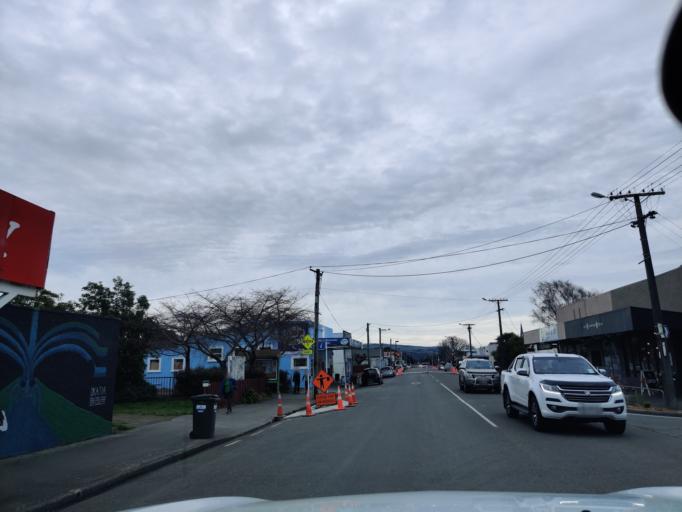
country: NZ
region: Manawatu-Wanganui
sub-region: Palmerston North City
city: Palmerston North
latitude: -40.2898
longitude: 175.7552
